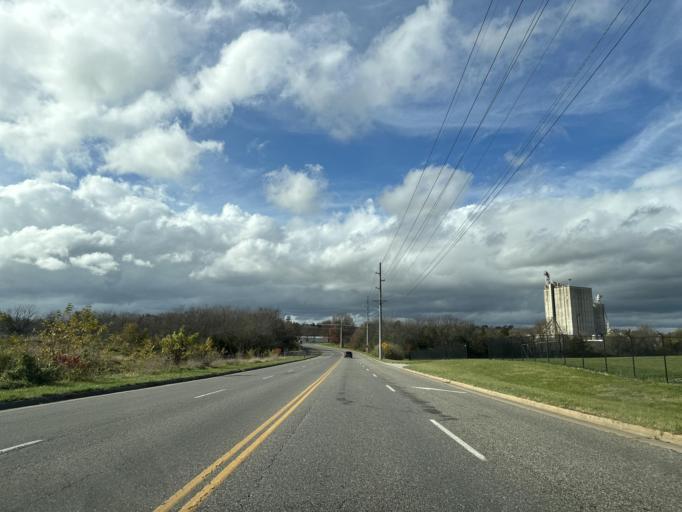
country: US
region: Virginia
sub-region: City of Harrisonburg
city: Harrisonburg
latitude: 38.4682
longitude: -78.8666
